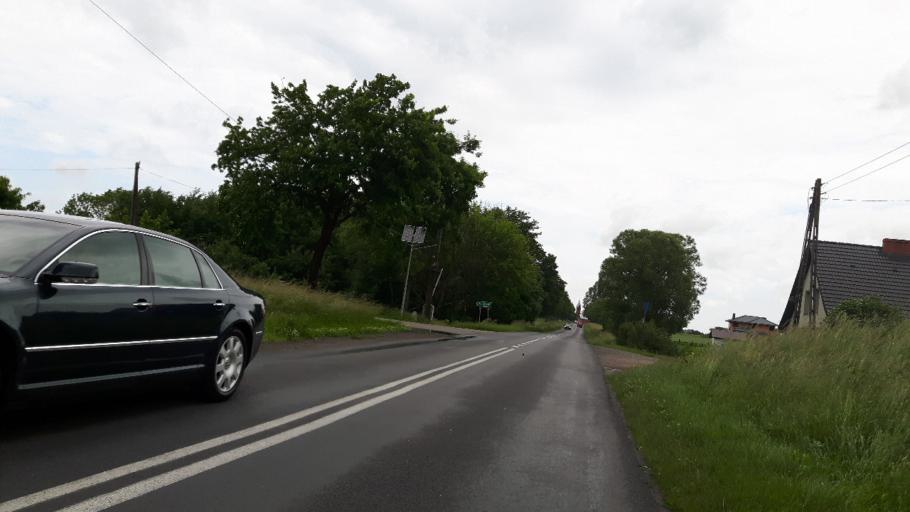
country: PL
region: West Pomeranian Voivodeship
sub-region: Powiat gryficki
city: Gryfice
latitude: 53.9709
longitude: 15.2331
